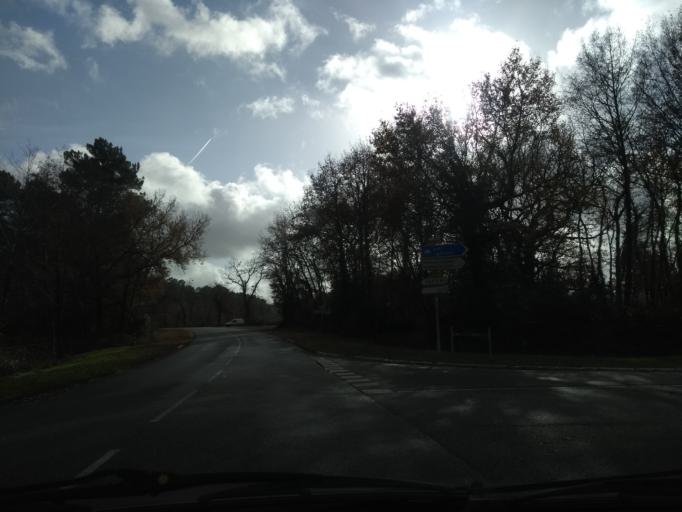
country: FR
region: Aquitaine
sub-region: Departement de la Gironde
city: Belin-Beliet
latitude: 44.4901
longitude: -0.7810
